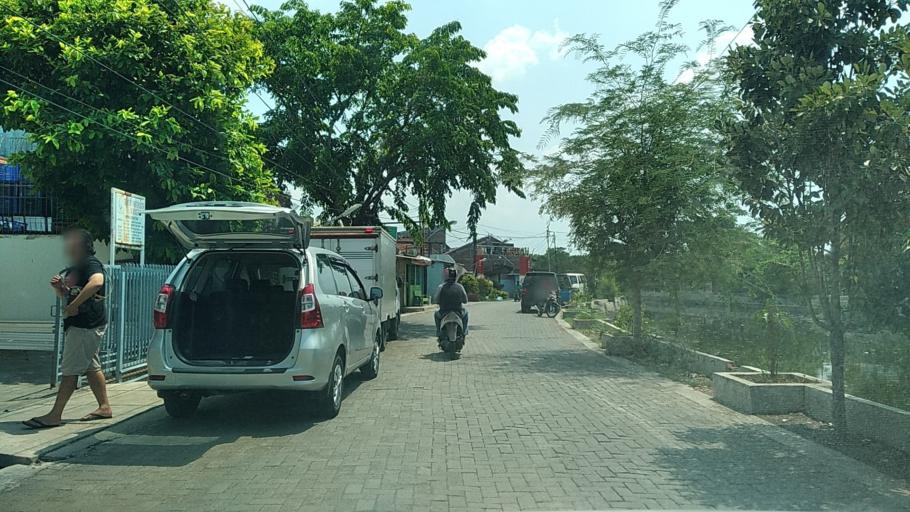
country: ID
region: Central Java
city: Semarang
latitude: -6.9670
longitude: 110.4399
